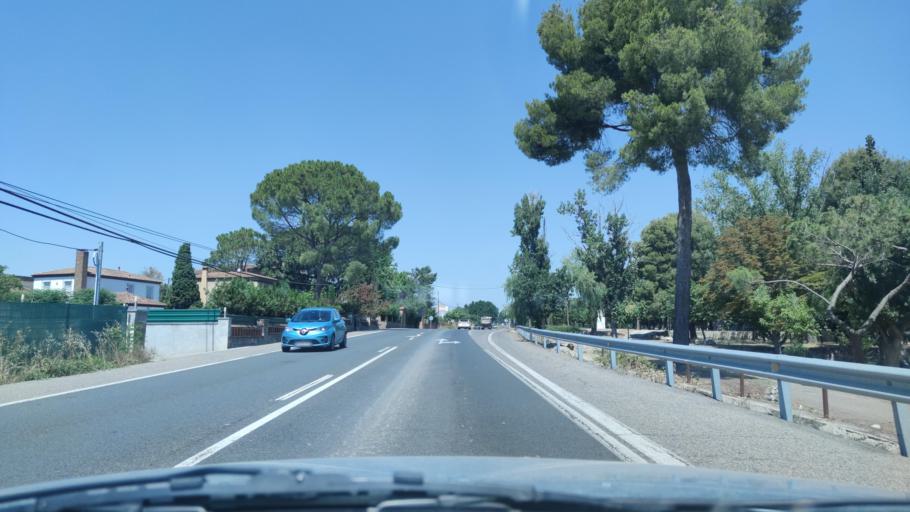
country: ES
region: Catalonia
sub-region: Provincia de Lleida
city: Alpicat
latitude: 41.6423
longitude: 0.5738
